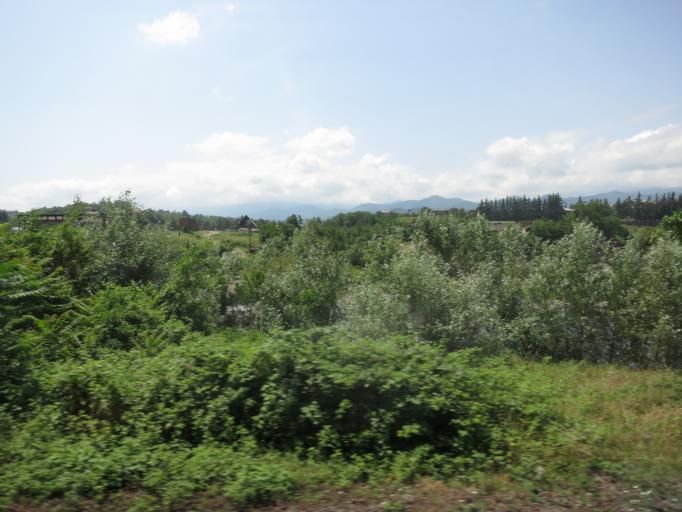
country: GE
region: Imereti
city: Zestap'oni
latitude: 42.1041
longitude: 43.0684
